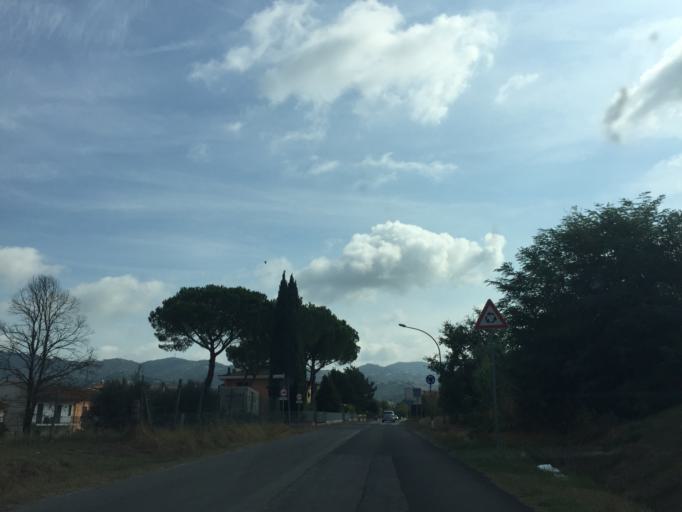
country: IT
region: Tuscany
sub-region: Provincia di Pistoia
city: Lamporecchio
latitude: 43.8177
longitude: 10.8727
